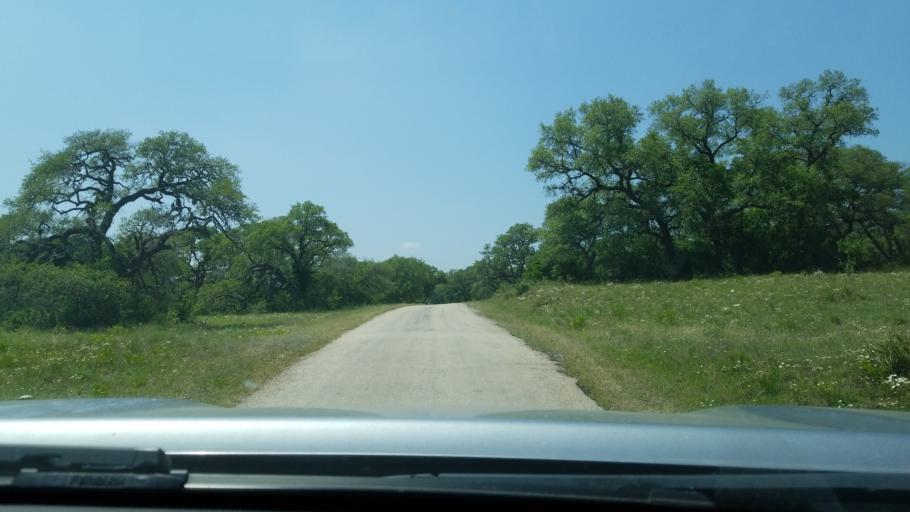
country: US
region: Texas
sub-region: Blanco County
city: Blanco
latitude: 30.0135
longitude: -98.4435
